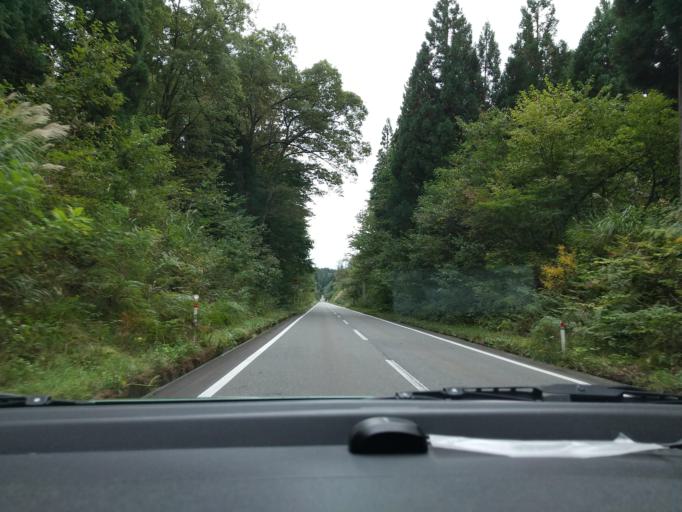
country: JP
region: Akita
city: Kakunodatemachi
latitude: 39.5664
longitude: 140.6364
